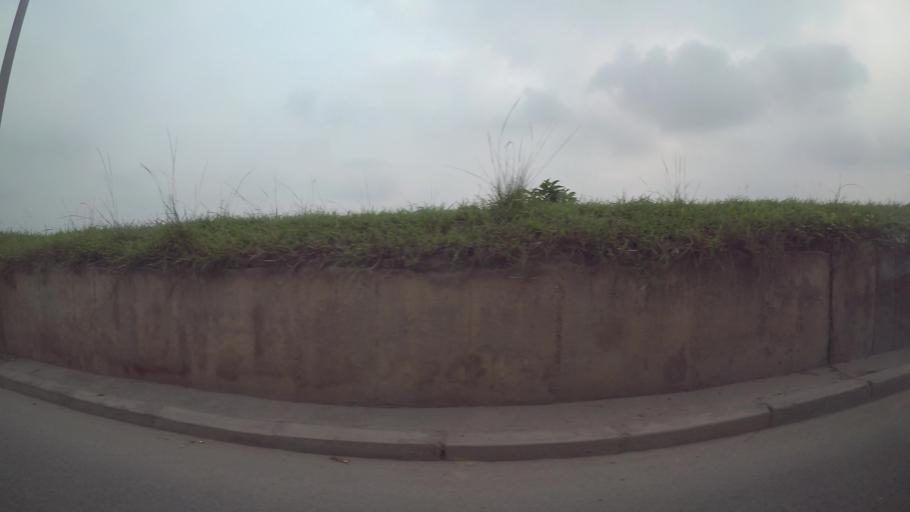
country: VN
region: Ha Noi
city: Trau Quy
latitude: 21.0745
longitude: 105.9149
